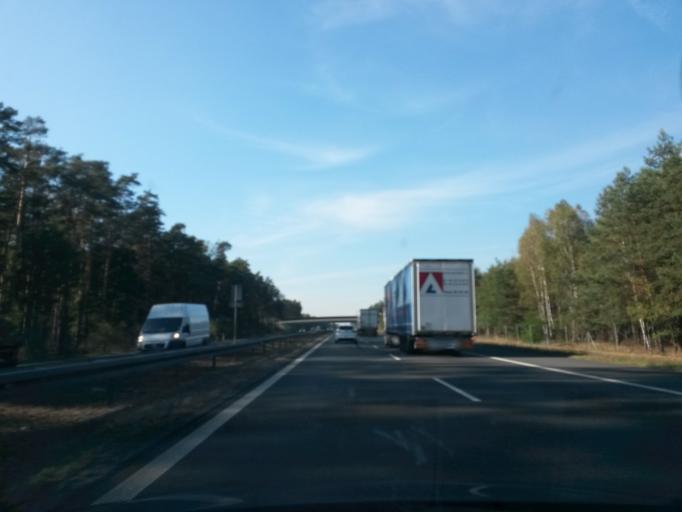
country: PL
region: Opole Voivodeship
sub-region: Powiat opolski
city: Dabrowa
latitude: 50.6214
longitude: 17.7605
